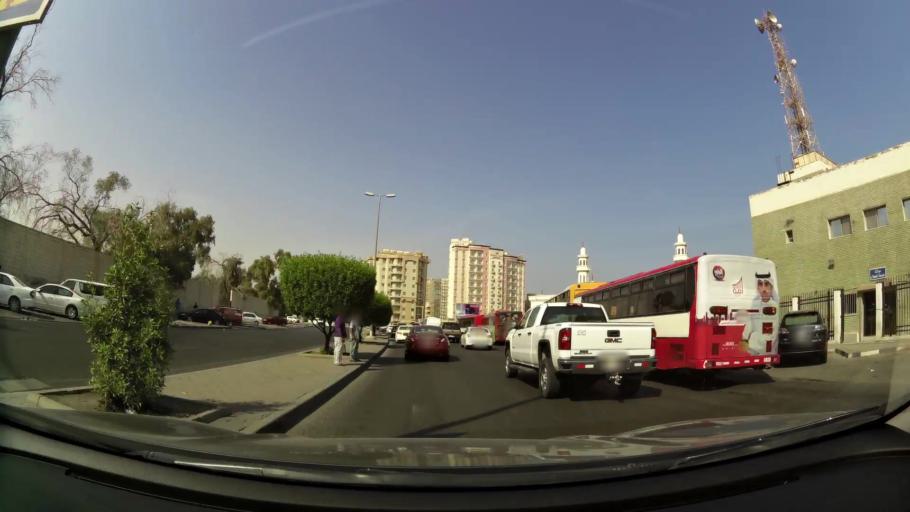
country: KW
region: Al Ahmadi
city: Al Fahahil
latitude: 29.0817
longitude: 48.1341
